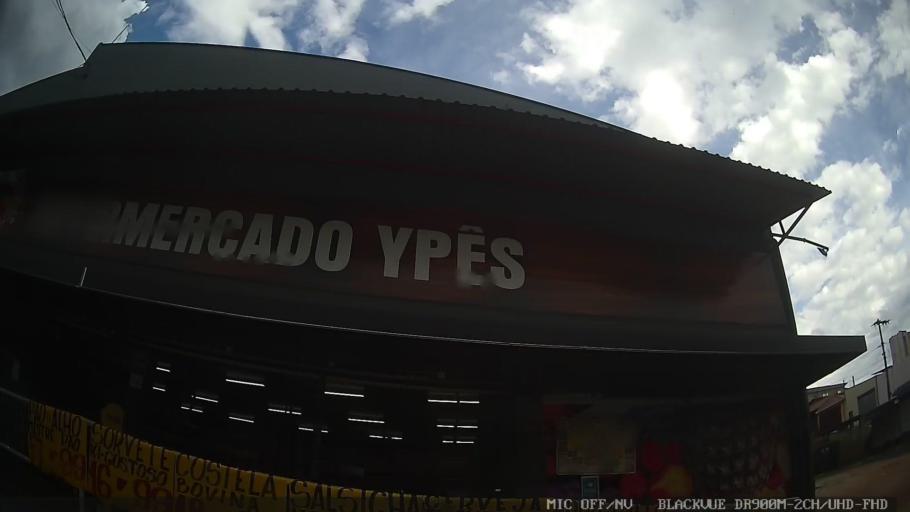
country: BR
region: Sao Paulo
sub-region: Pedreira
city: Pedreira
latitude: -22.7230
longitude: -46.8932
